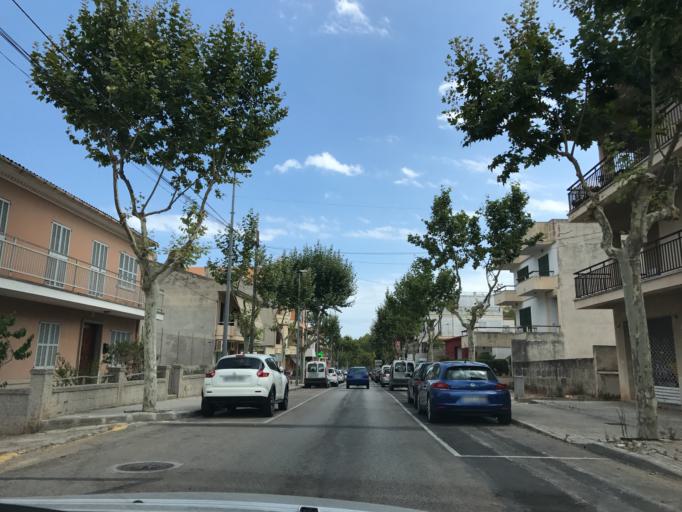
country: ES
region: Balearic Islands
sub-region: Illes Balears
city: Son Servera
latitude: 39.6193
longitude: 3.3629
